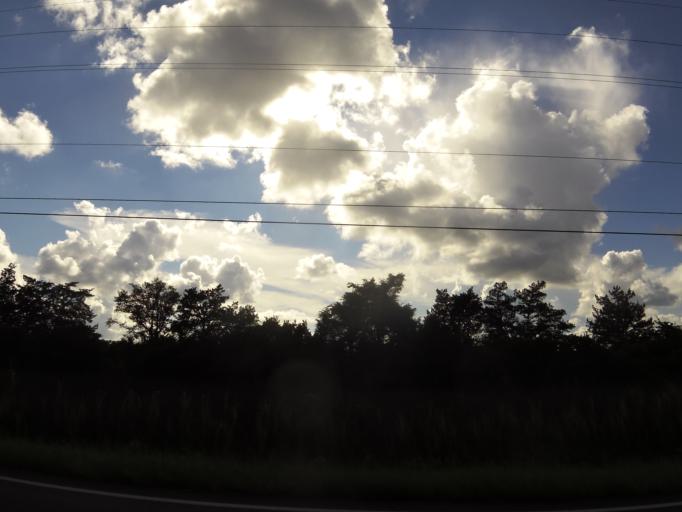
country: US
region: Georgia
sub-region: Camden County
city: Woodbine
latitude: 31.0387
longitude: -81.7301
